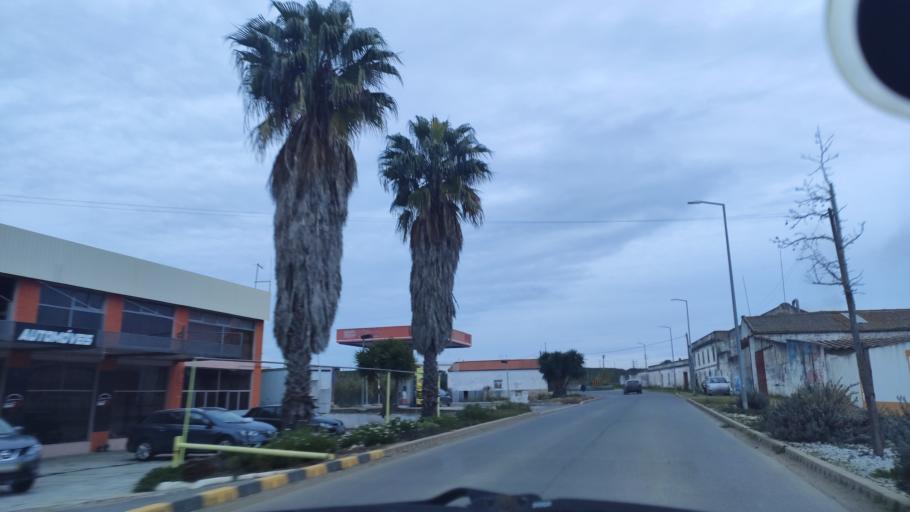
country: PT
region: Beja
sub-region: Beja
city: Ferreira do Alentejo
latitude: 38.0589
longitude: -8.1091
